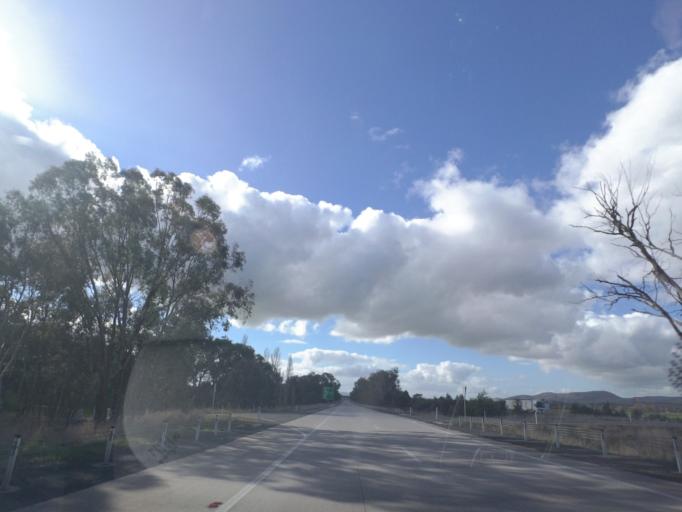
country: AU
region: New South Wales
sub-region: Greater Hume Shire
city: Holbrook
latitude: -35.7469
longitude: 147.2993
